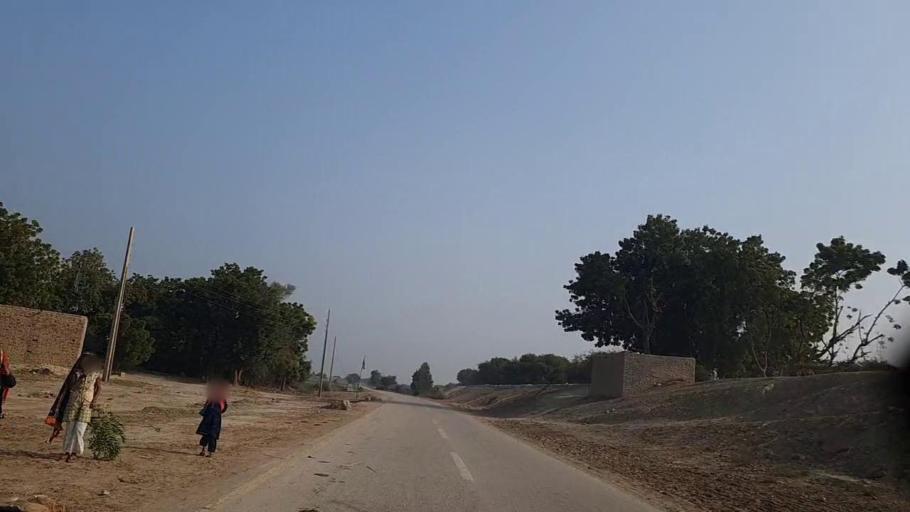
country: PK
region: Sindh
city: Sann
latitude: 26.1534
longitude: 68.1206
